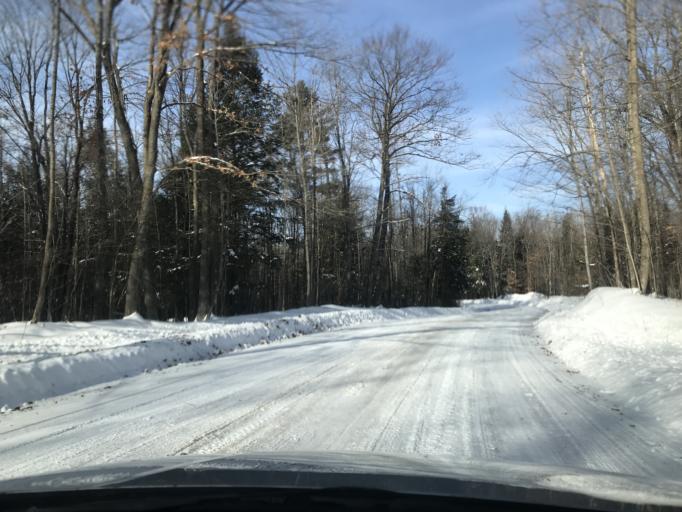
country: US
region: Wisconsin
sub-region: Oconto County
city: Gillett
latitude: 45.1467
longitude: -88.2350
